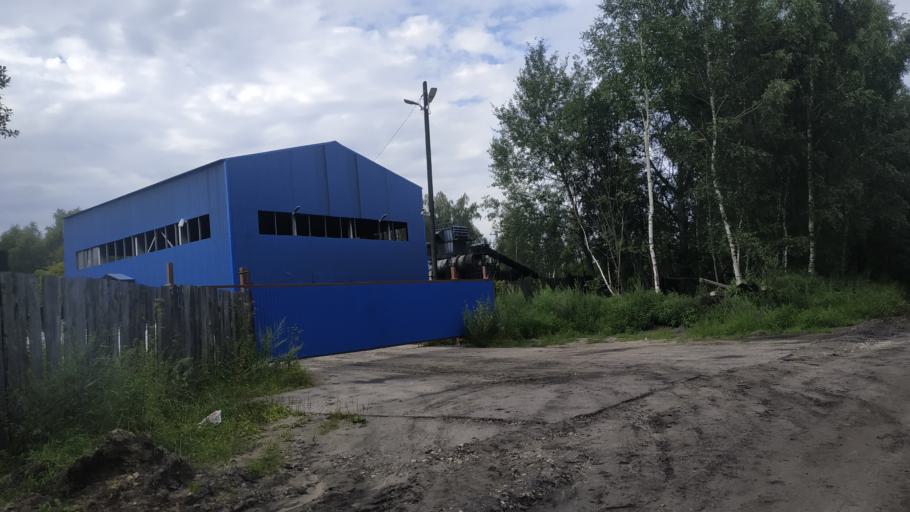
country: RU
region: Moskovskaya
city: Radovitskiy
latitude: 55.1411
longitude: 39.5527
